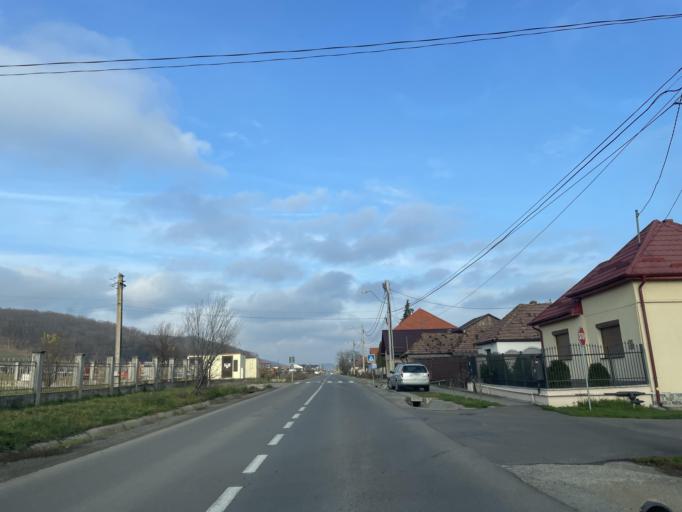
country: RO
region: Mures
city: Reghin-Sat
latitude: 46.7898
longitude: 24.7031
